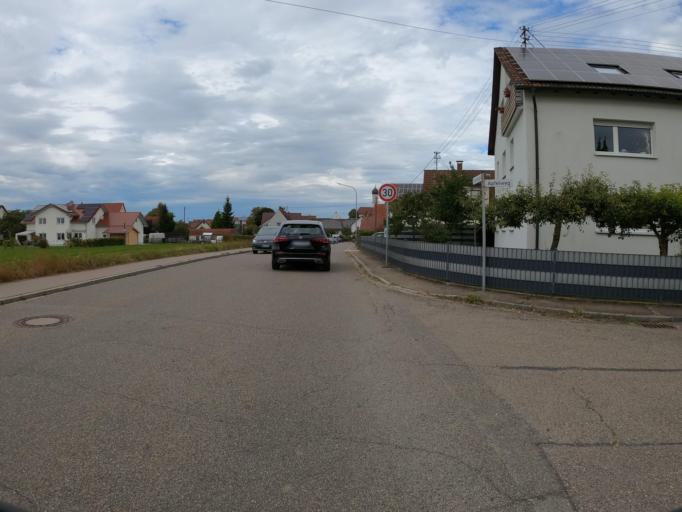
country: DE
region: Bavaria
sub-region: Swabia
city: Holzheim
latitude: 48.3794
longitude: 10.0766
